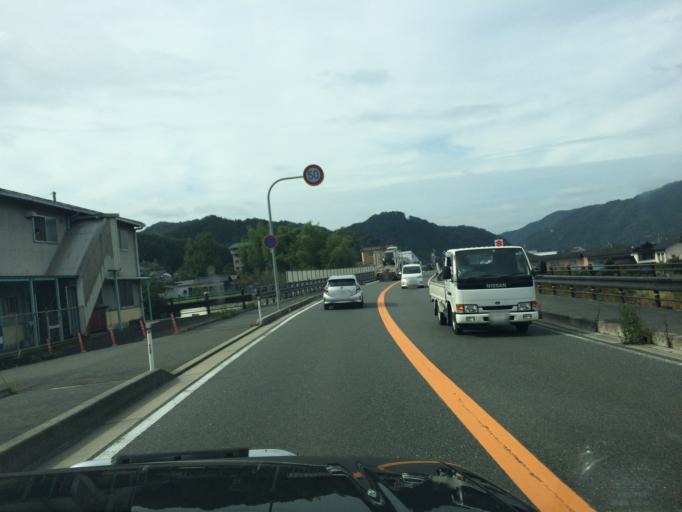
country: JP
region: Hyogo
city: Toyooka
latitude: 35.3400
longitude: 134.8438
